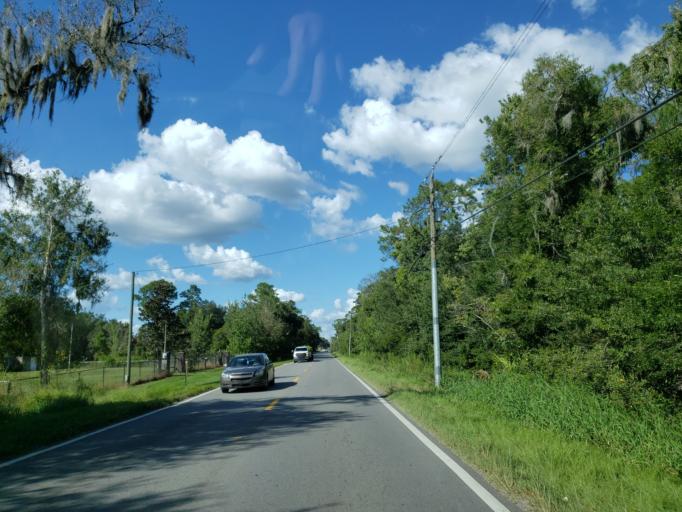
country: US
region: Florida
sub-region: Hillsborough County
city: Dover
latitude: 27.9814
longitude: -82.1869
